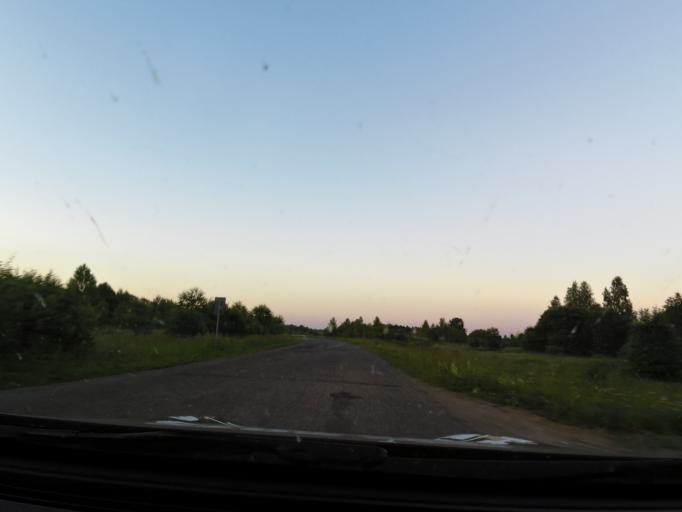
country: RU
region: Kostroma
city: Buy
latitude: 58.3529
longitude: 41.1790
